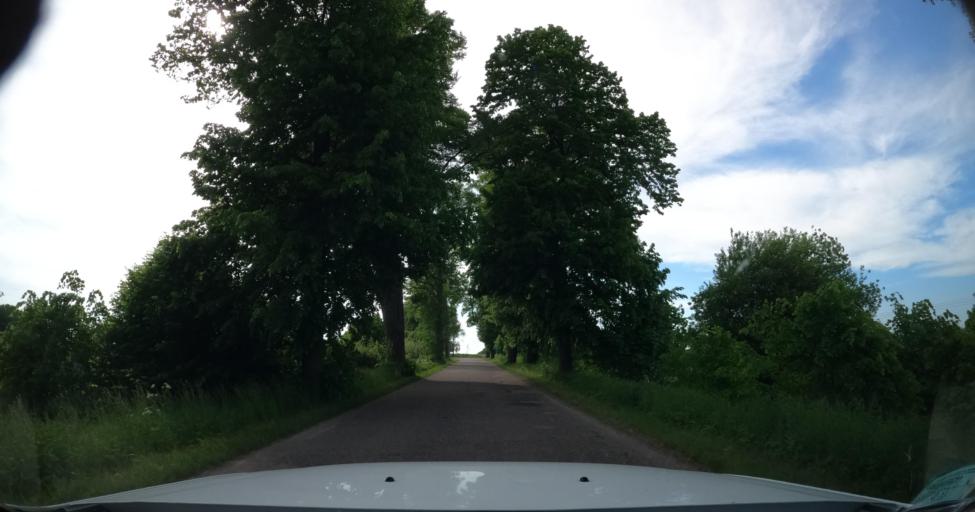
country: PL
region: Warmian-Masurian Voivodeship
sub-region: Powiat ostrodzki
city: Milakowo
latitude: 54.0174
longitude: 20.0517
